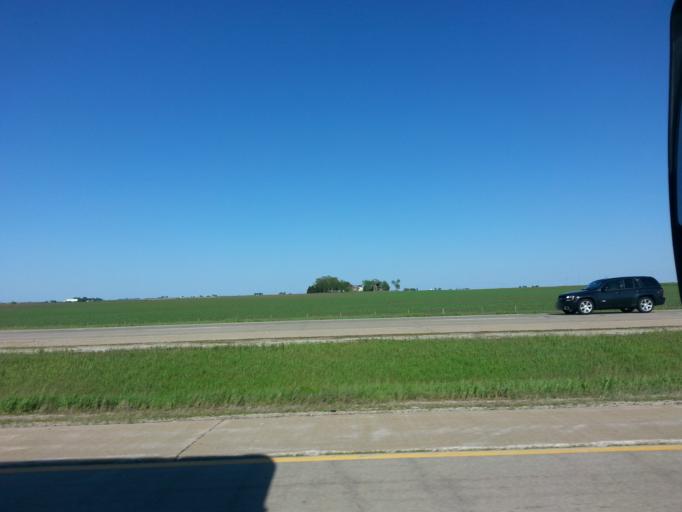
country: US
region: Illinois
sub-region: Marshall County
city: Wenona
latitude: 41.1648
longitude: -89.0759
